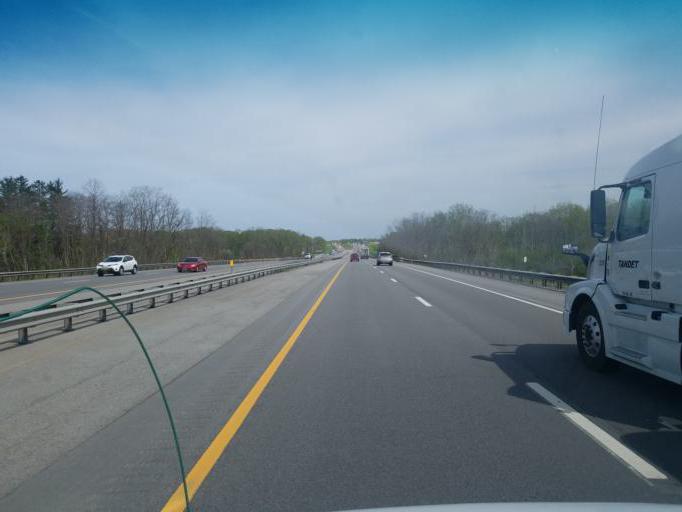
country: US
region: New York
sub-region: Monroe County
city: Scottsville
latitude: 43.0437
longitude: -77.7306
